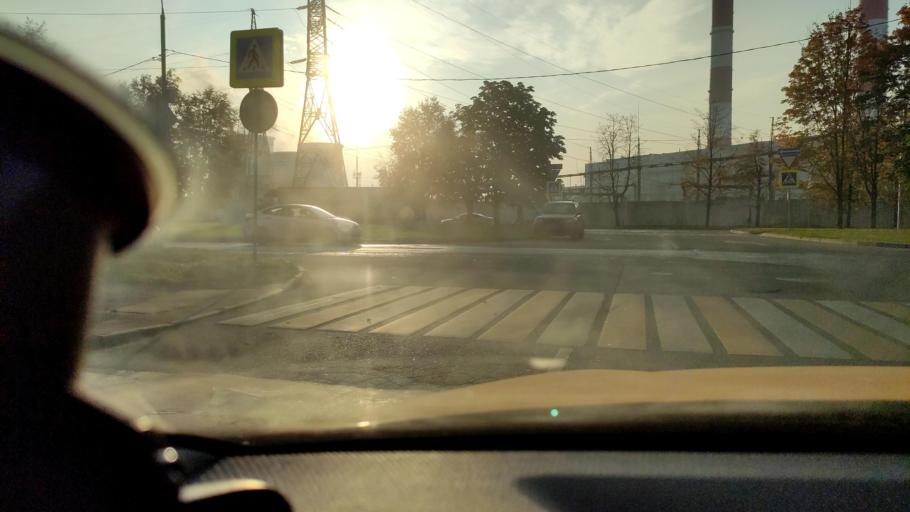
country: RU
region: Moscow
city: Metrogorodok
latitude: 55.8249
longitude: 37.7671
